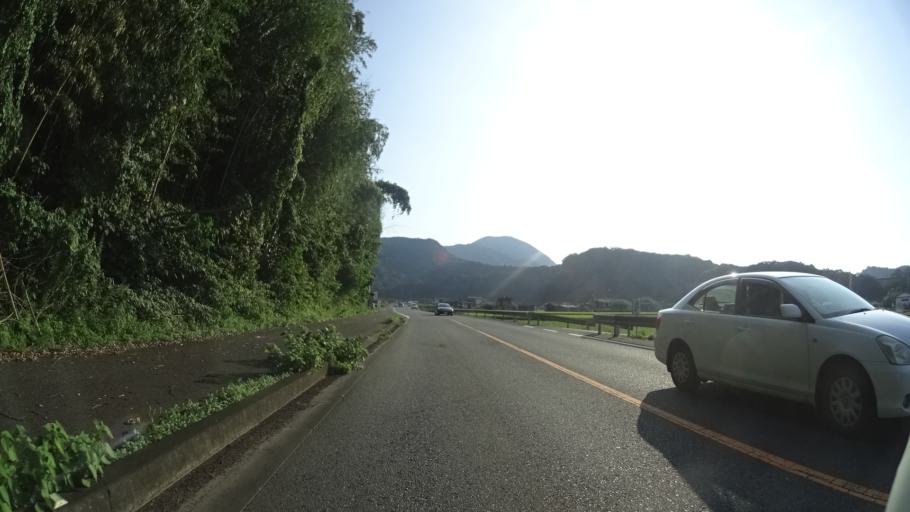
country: JP
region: Oita
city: Bungo-Takada-shi
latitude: 33.5014
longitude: 131.3272
